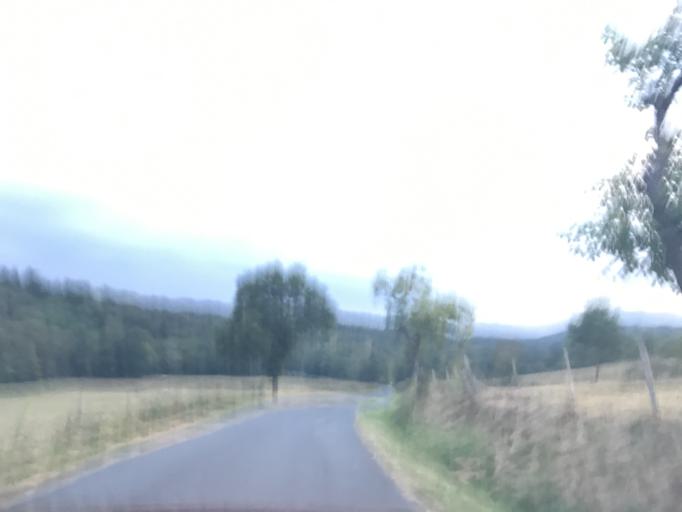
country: FR
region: Auvergne
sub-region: Departement du Puy-de-Dome
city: Escoutoux
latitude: 45.7907
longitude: 3.5748
